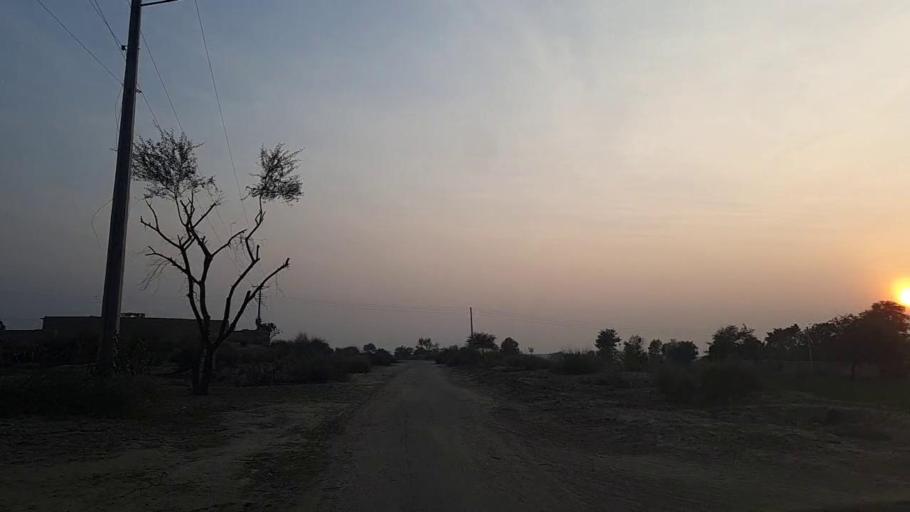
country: PK
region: Sindh
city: Jam Sahib
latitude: 26.4615
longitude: 68.5520
